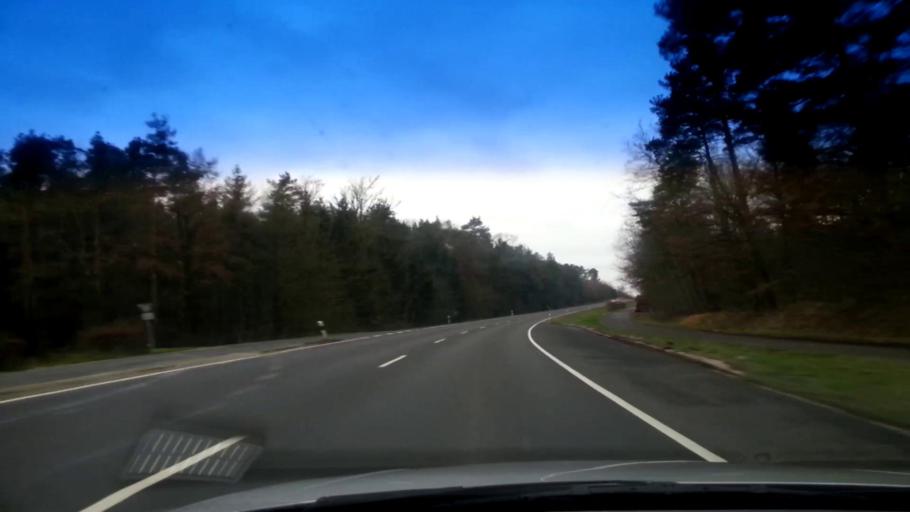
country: DE
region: Bavaria
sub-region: Upper Franconia
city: Stegaurach
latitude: 49.8364
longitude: 10.8169
